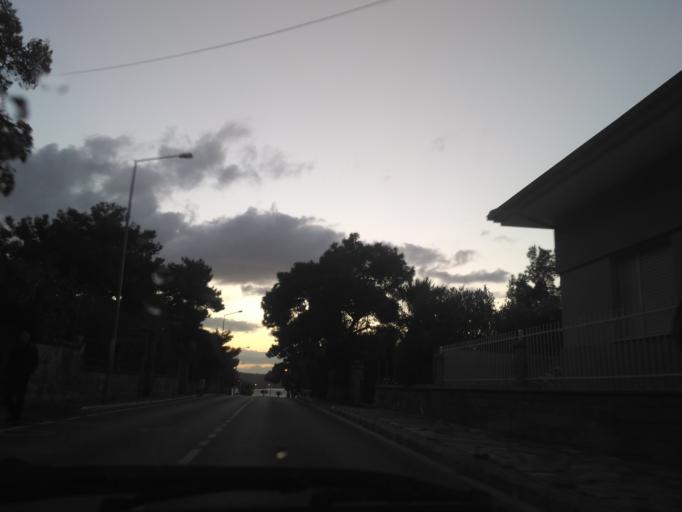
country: TR
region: Balikesir
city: Ayvalik
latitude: 39.3068
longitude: 26.6674
